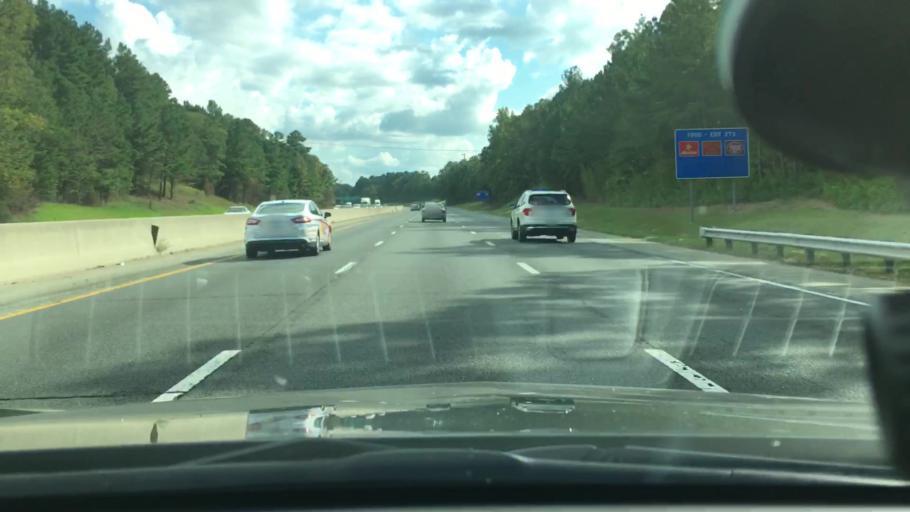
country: US
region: North Carolina
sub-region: Orange County
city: Chapel Hill
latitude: 35.9225
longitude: -78.9859
